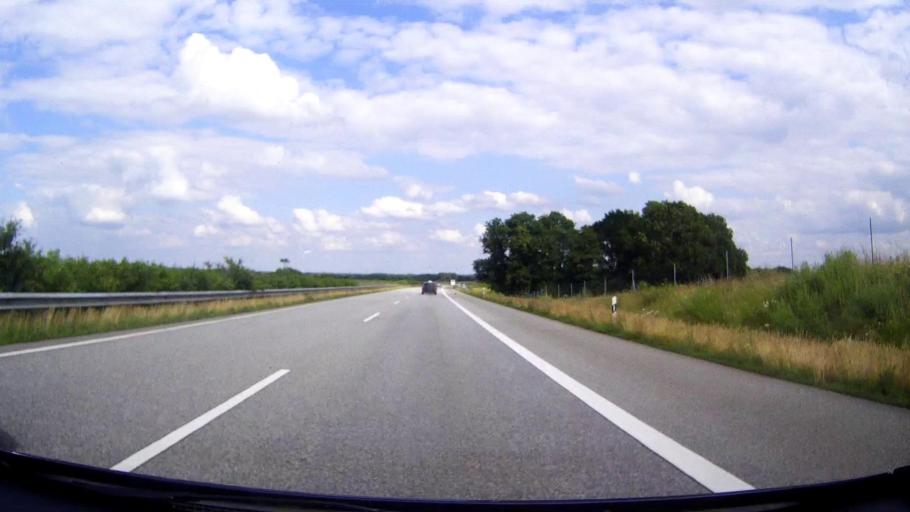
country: DE
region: Schleswig-Holstein
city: Monkhagen
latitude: 53.9154
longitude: 10.5265
